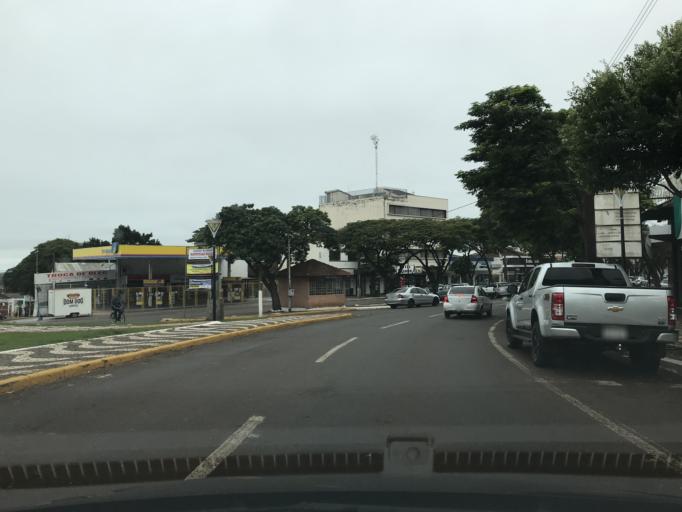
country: PY
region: Canindeyu
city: Salto del Guaira
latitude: -24.0812
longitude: -54.2544
